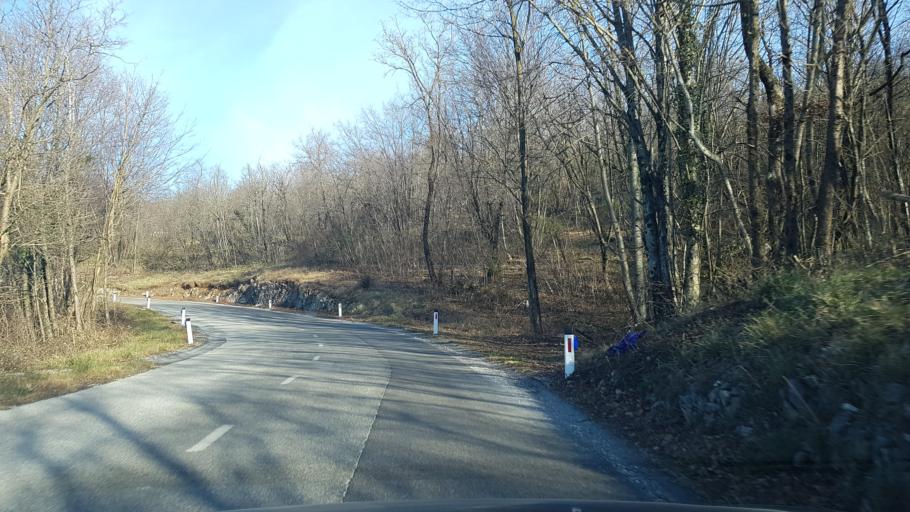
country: SI
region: Nova Gorica
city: Kromberk
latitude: 46.0024
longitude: 13.6861
